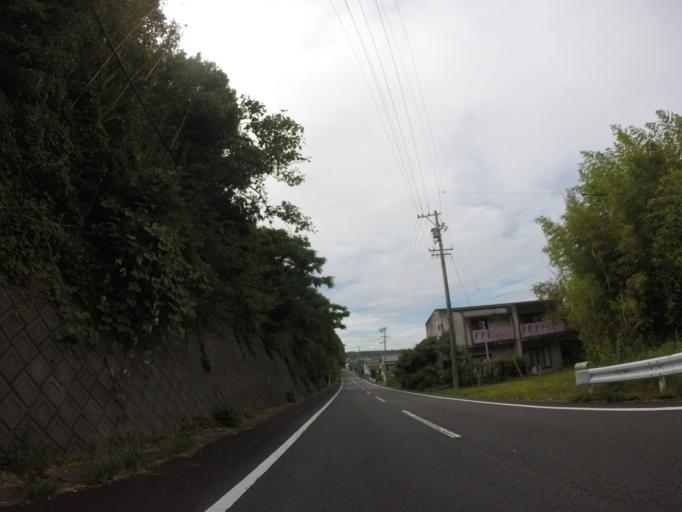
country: JP
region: Shizuoka
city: Oyama
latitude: 34.6279
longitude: 138.1979
